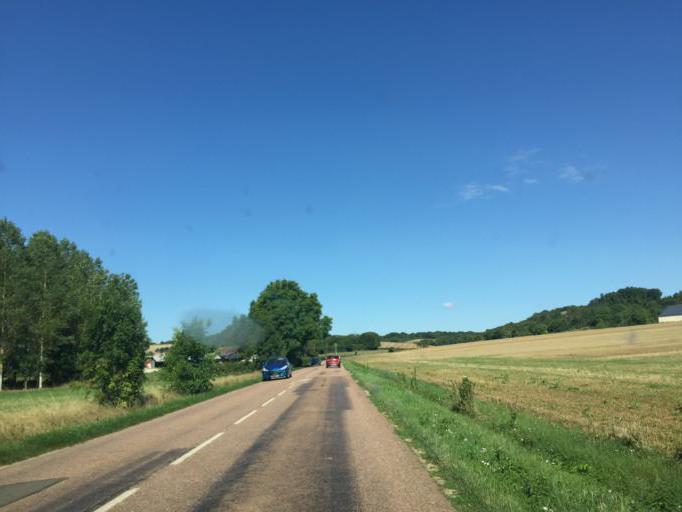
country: FR
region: Bourgogne
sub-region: Departement de l'Yonne
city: Fontenailles
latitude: 47.4787
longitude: 3.4285
